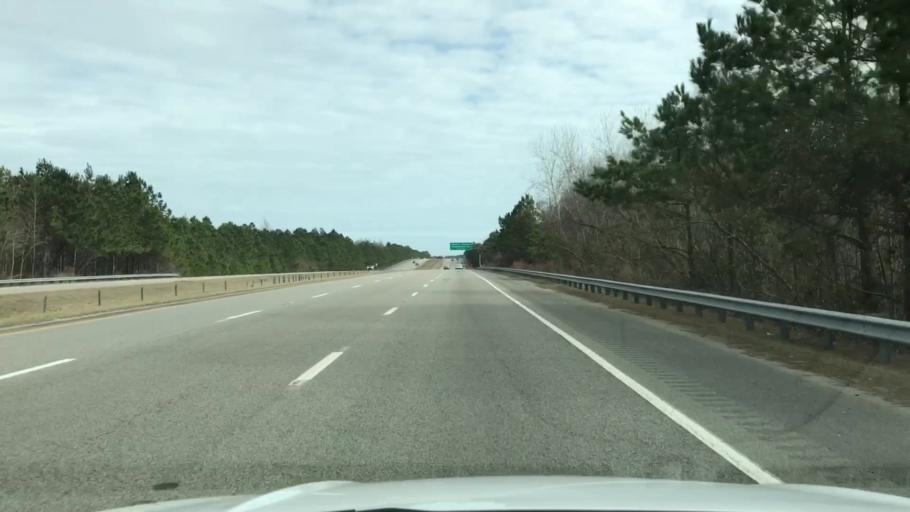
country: US
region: South Carolina
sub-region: Horry County
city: Myrtle Beach
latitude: 33.7491
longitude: -78.8770
